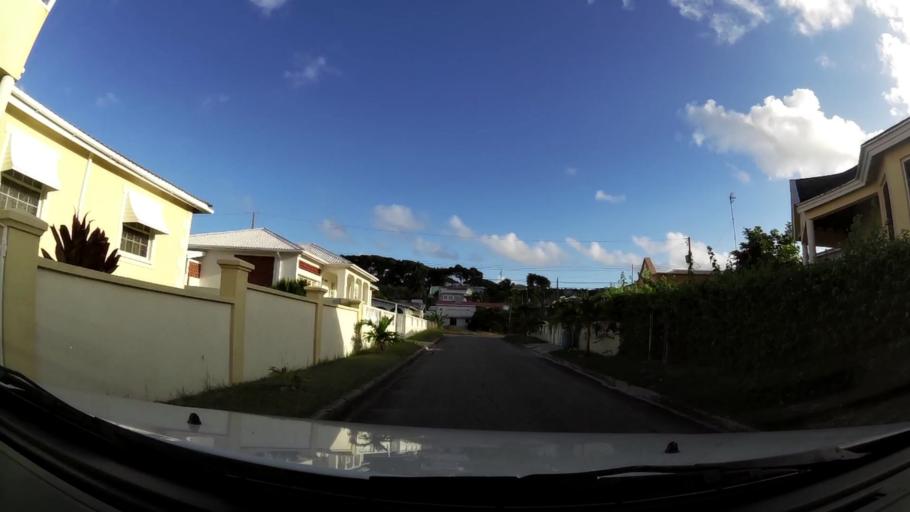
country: BB
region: Christ Church
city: Oistins
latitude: 13.0677
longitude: -59.5524
